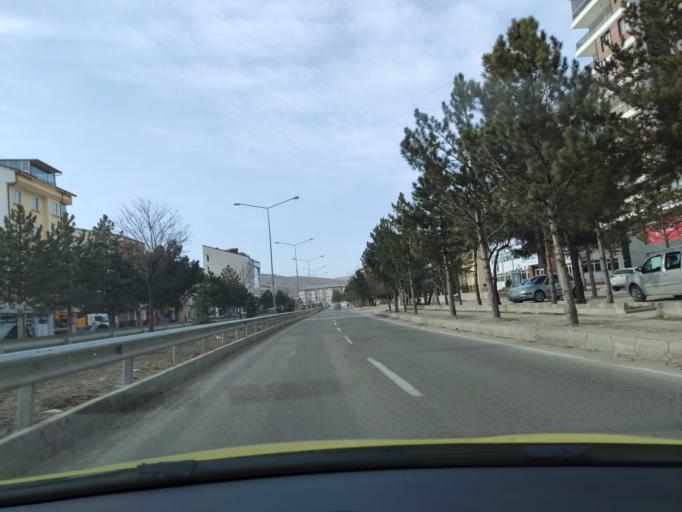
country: TR
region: Bayburt
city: Bayburt
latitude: 40.2460
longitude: 40.2339
